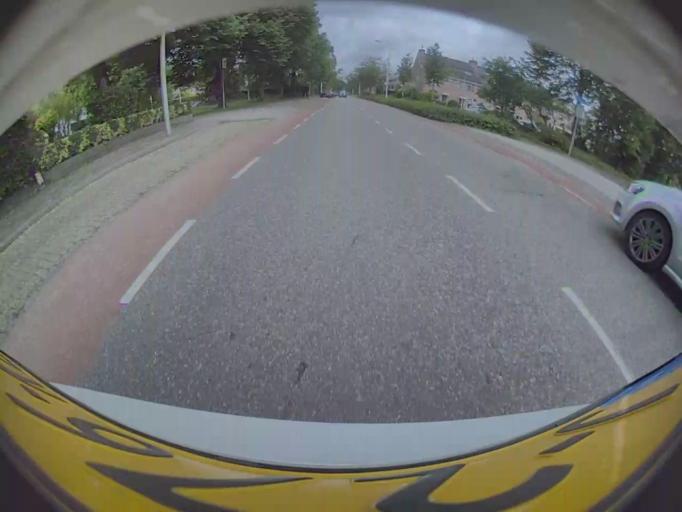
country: NL
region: South Holland
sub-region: Gemeente Voorschoten
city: Voorschoten
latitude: 52.1190
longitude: 4.4368
